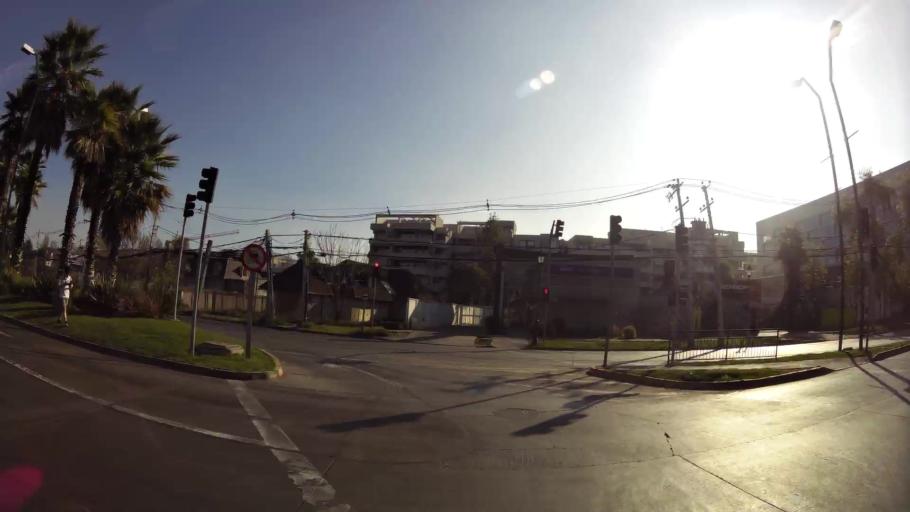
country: CL
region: Santiago Metropolitan
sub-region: Provincia de Santiago
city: Villa Presidente Frei, Nunoa, Santiago, Chile
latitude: -33.3562
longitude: -70.5173
